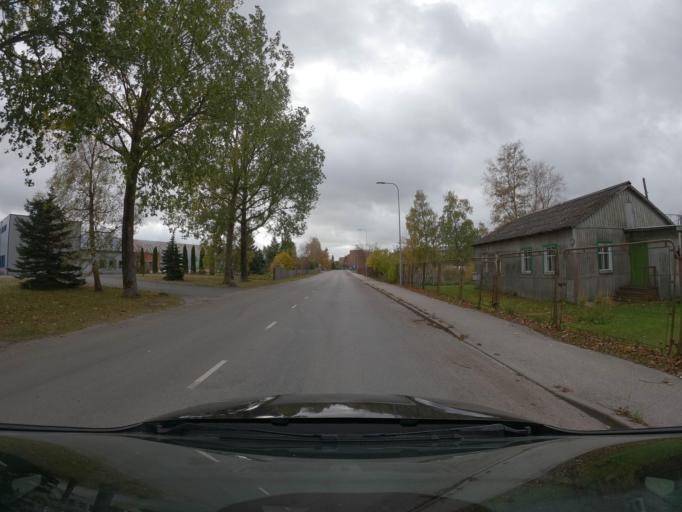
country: EE
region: Saare
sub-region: Kuressaare linn
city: Kuressaare
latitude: 58.2648
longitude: 22.4928
